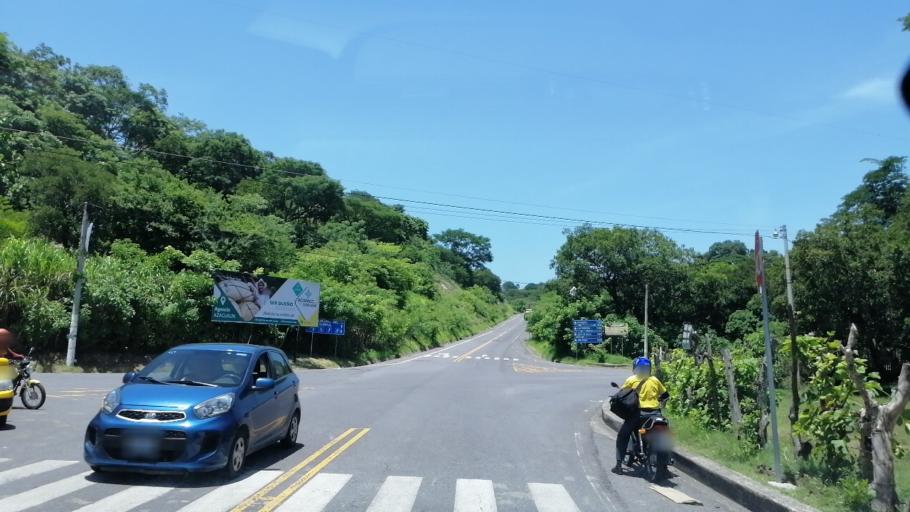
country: SV
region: Chalatenango
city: Chalatenango
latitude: 14.0284
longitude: -88.9394
